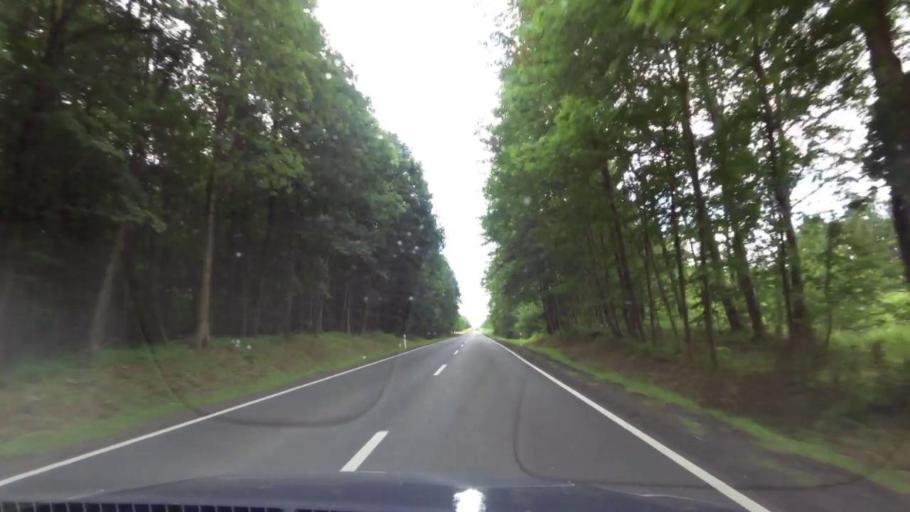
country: PL
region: West Pomeranian Voivodeship
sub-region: Powiat mysliborski
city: Mysliborz
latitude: 52.9676
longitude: 14.7437
